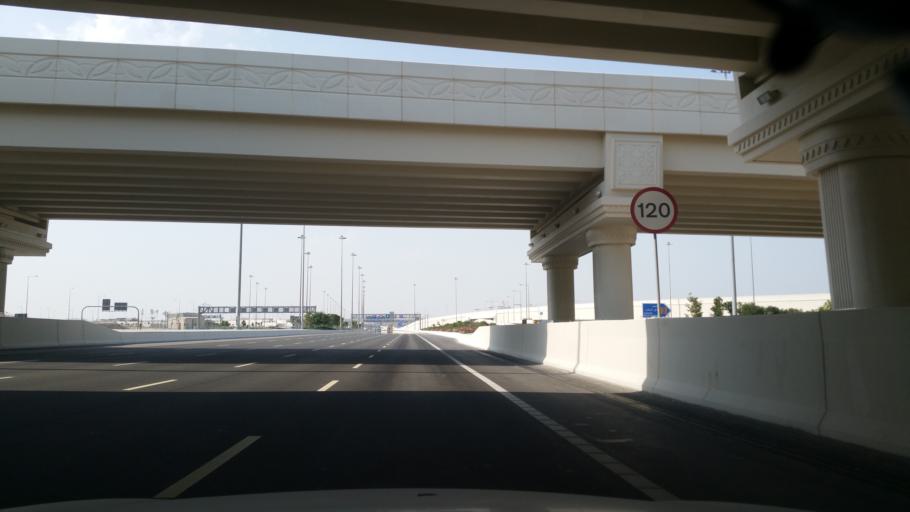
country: QA
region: Baladiyat Umm Salal
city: Umm Salal Muhammad
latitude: 25.3935
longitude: 51.4971
